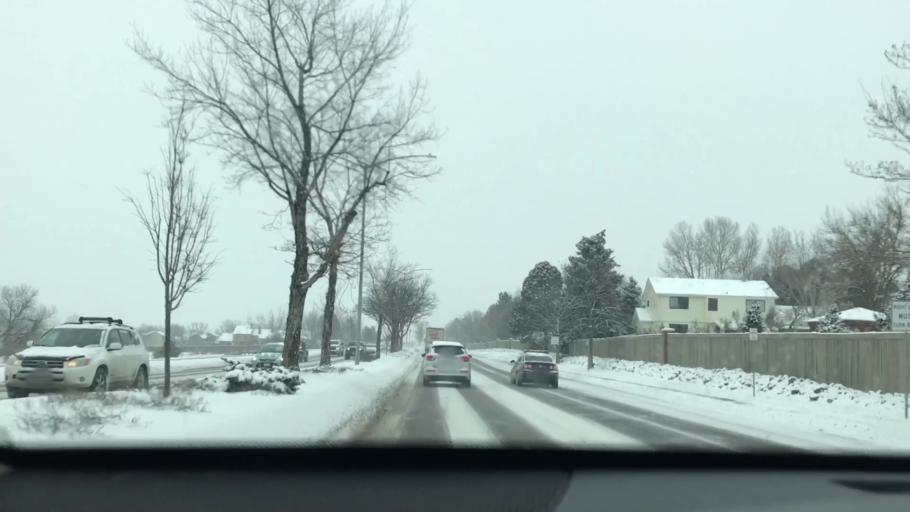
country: US
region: Colorado
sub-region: Adams County
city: Westminster
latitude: 39.8754
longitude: -105.0531
